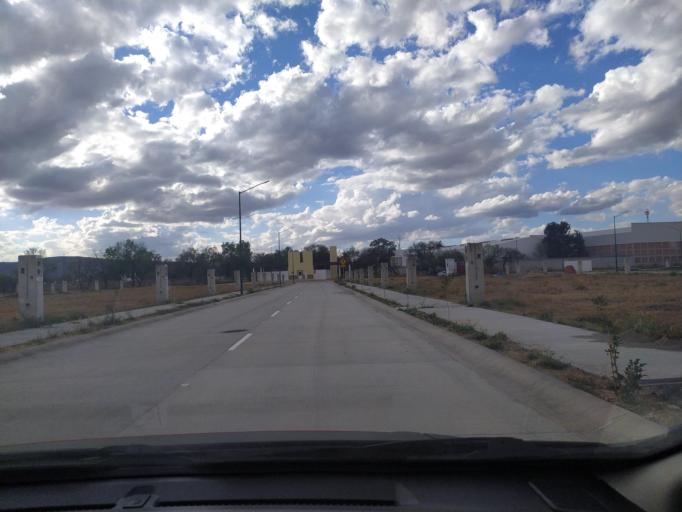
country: LA
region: Oudomxai
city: Muang La
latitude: 21.0240
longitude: 101.8234
